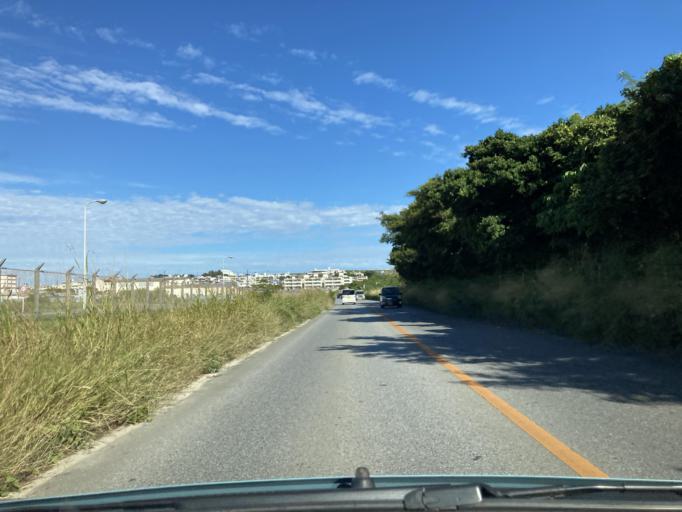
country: JP
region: Okinawa
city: Okinawa
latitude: 26.3752
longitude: 127.7459
